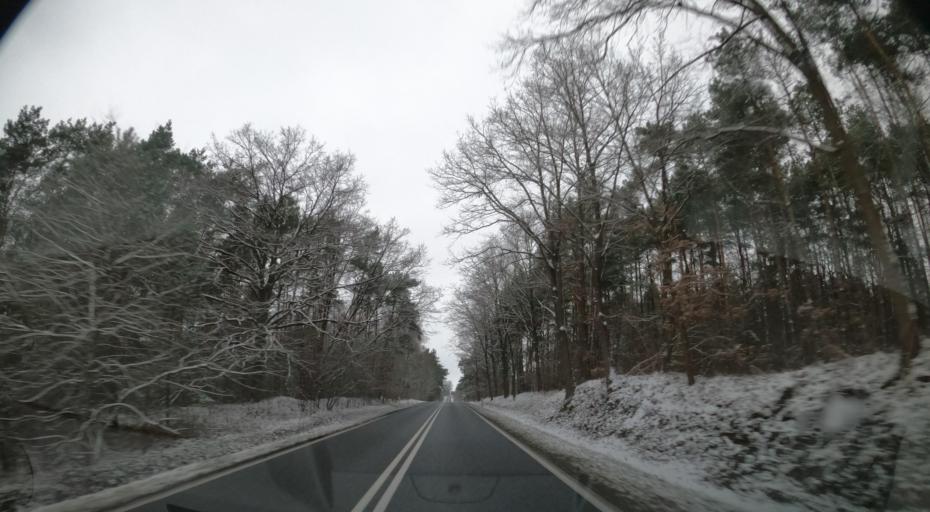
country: PL
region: Masovian Voivodeship
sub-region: Powiat plocki
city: Nowy Duninow
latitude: 52.5849
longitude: 19.5214
